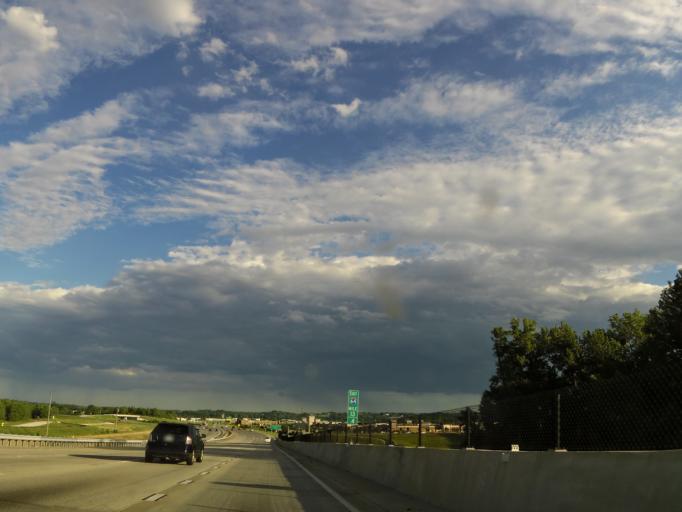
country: US
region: Missouri
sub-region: Saint Charles County
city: Weldon Spring
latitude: 38.6837
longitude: -90.6621
